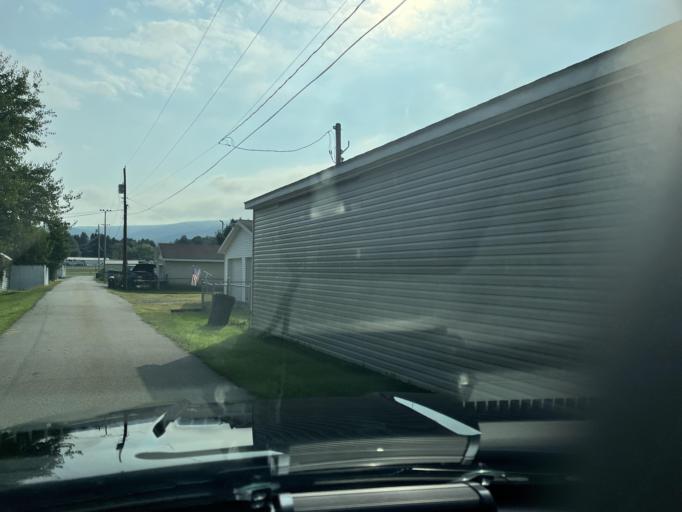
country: US
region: Pennsylvania
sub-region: Fayette County
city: Leith-Hatfield
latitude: 39.8724
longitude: -79.7168
